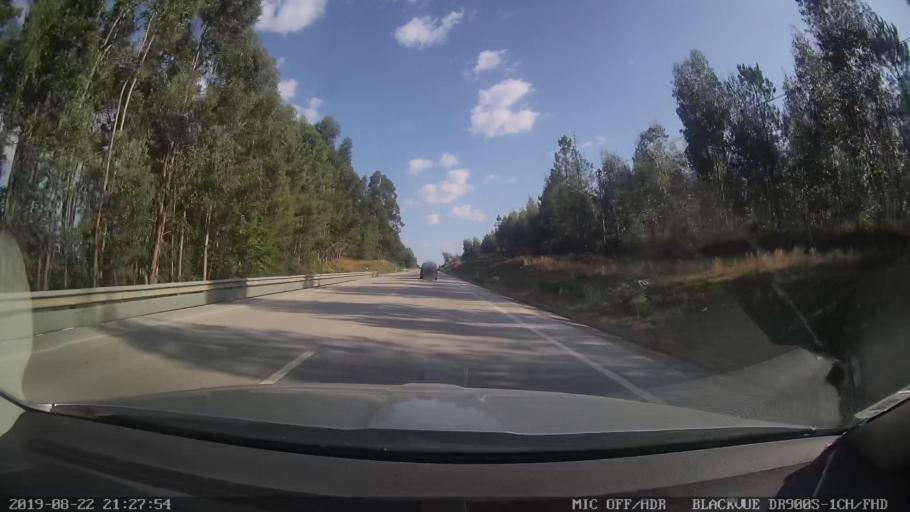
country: PT
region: Leiria
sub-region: Pedrogao Grande
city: Pedrogao Grande
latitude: 39.8851
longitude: -8.1203
